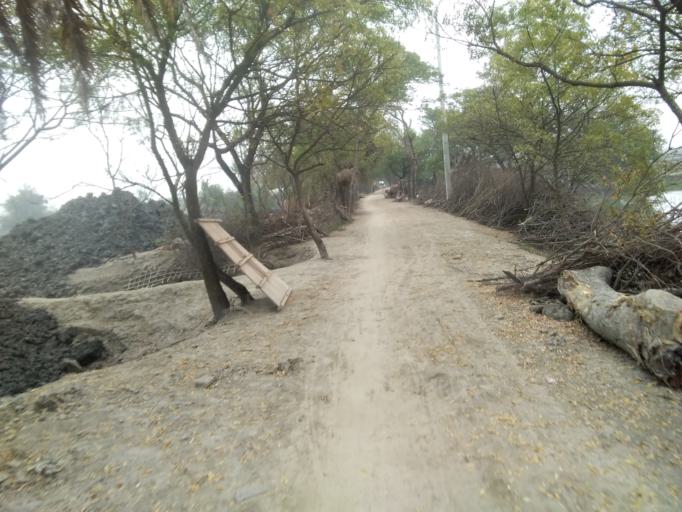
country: BD
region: Khulna
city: Satkhira
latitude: 22.5710
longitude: 89.0785
